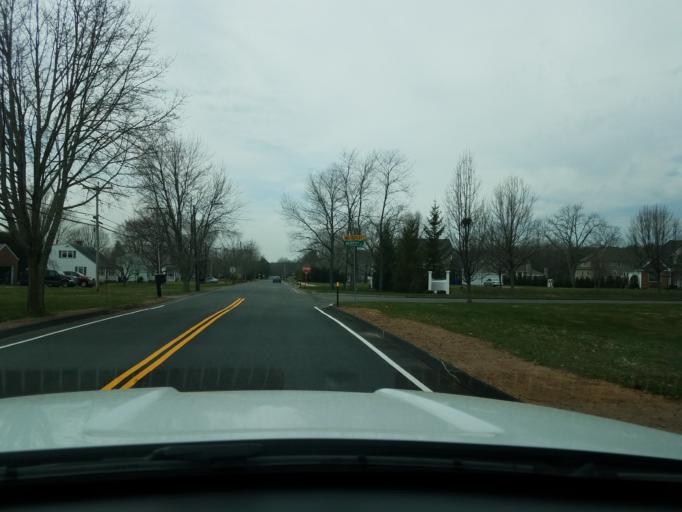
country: US
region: Connecticut
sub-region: Hartford County
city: Newington
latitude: 41.6490
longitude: -72.6840
